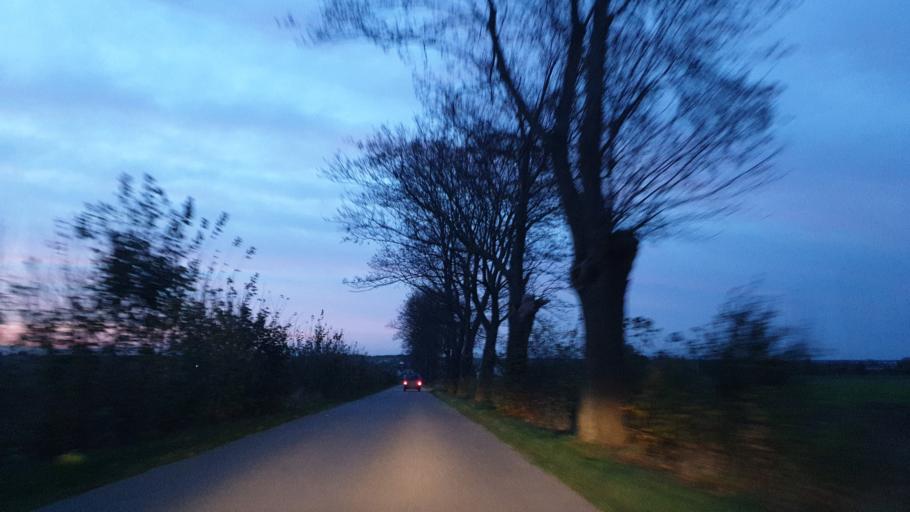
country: PL
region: Pomeranian Voivodeship
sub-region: Powiat pucki
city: Krokowa
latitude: 54.7803
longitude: 18.2030
